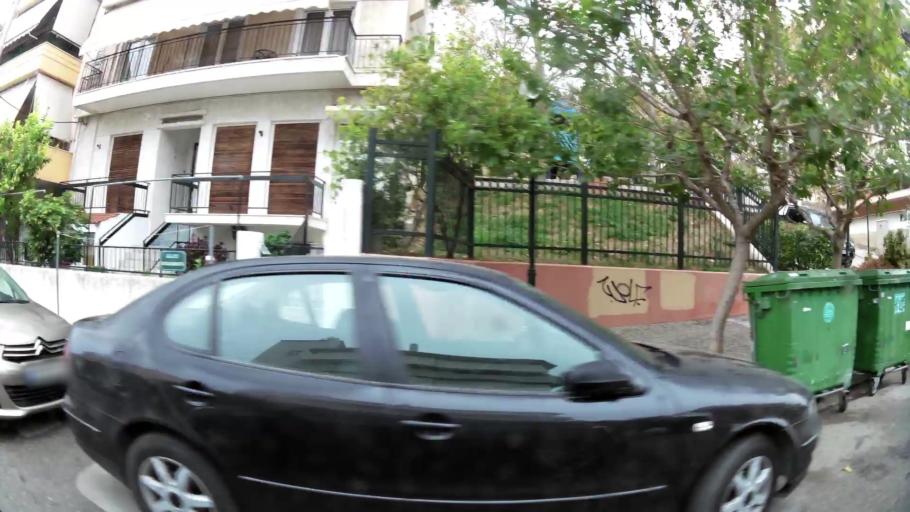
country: GR
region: Attica
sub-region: Nomos Piraios
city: Korydallos
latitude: 37.9909
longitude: 23.6494
